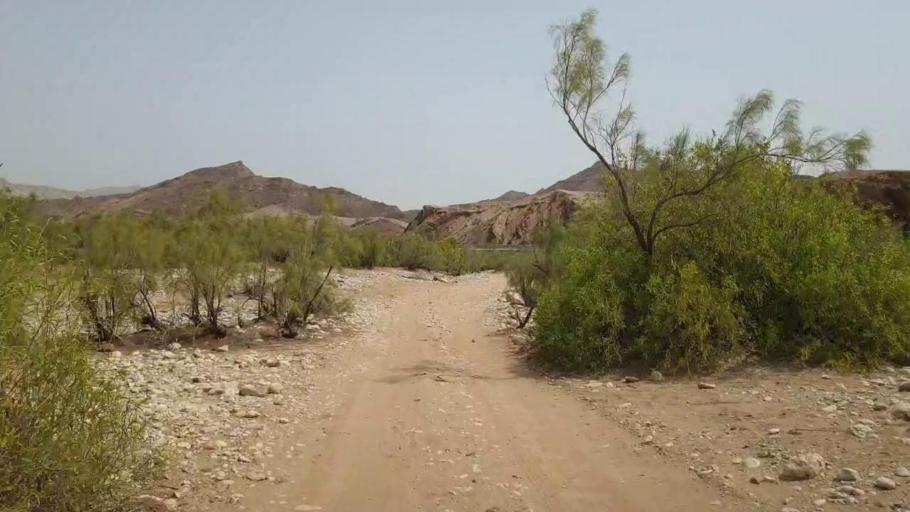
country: PK
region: Sindh
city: Sann
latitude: 25.8838
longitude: 67.9218
